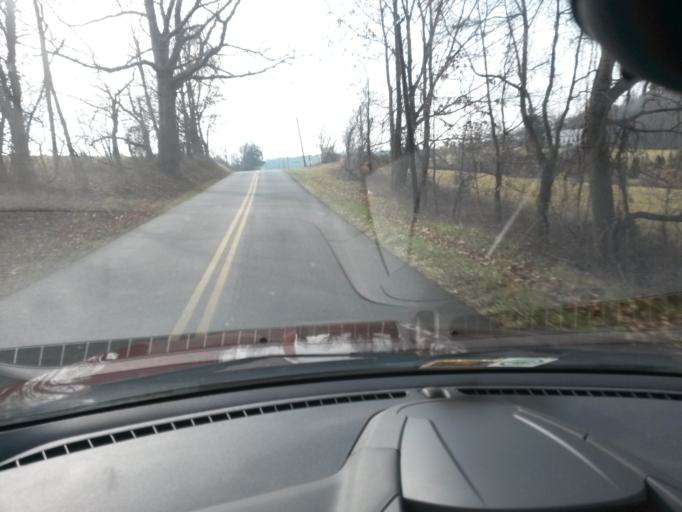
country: US
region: Virginia
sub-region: Botetourt County
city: Fincastle
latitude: 37.5698
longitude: -79.8825
